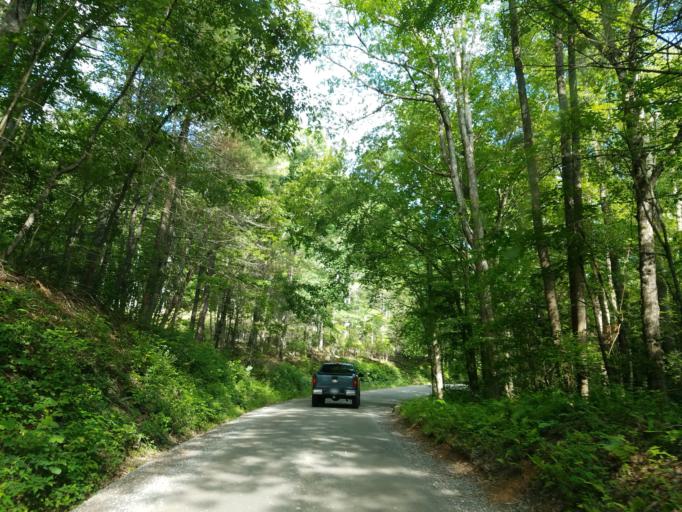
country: US
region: Georgia
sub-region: Fannin County
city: Blue Ridge
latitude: 34.7849
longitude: -84.2390
